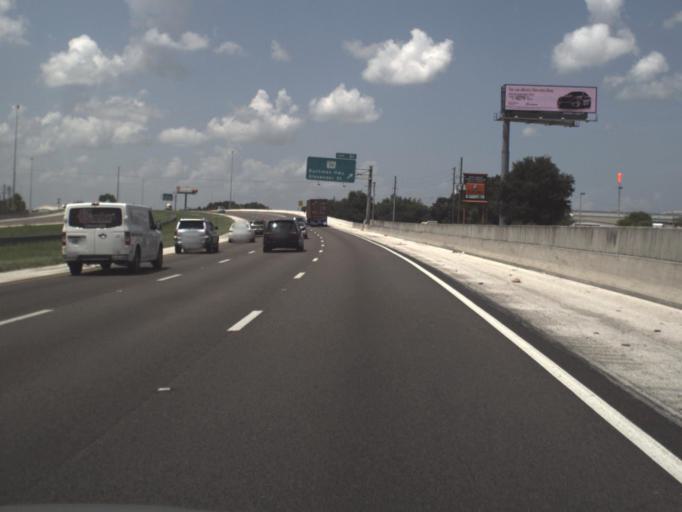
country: US
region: Florida
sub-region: Hillsborough County
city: Plant City
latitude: 28.0370
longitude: -82.1191
